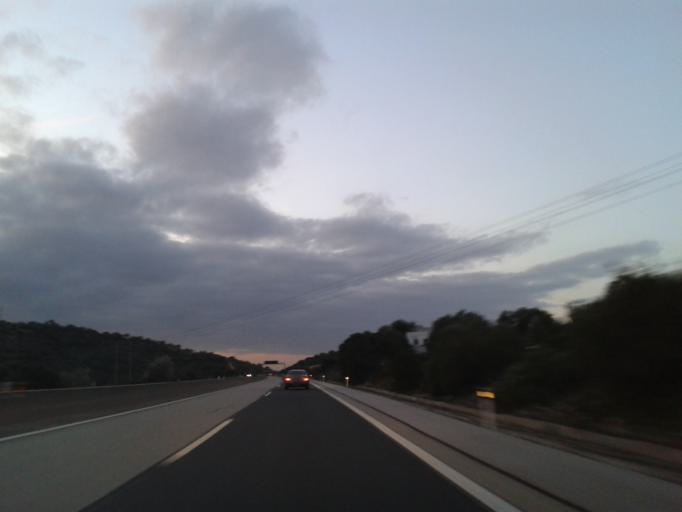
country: PT
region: Faro
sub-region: Loule
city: Boliqueime
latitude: 37.1511
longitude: -8.1703
